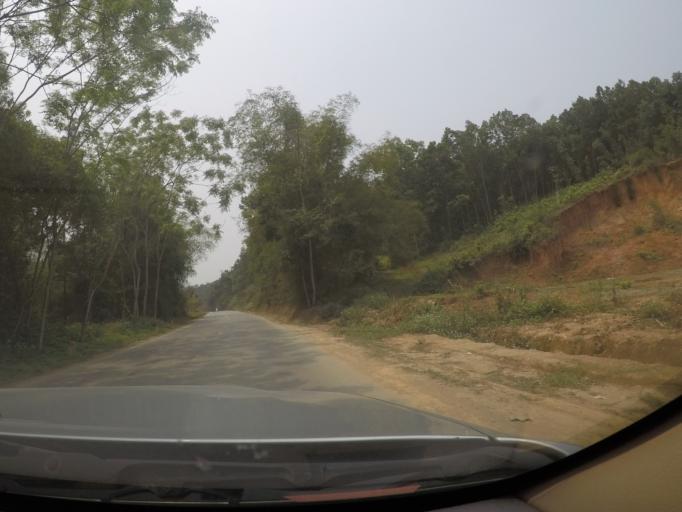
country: VN
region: Thanh Hoa
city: Thi Tran Ngoc Lac
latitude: 20.1250
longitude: 105.3891
